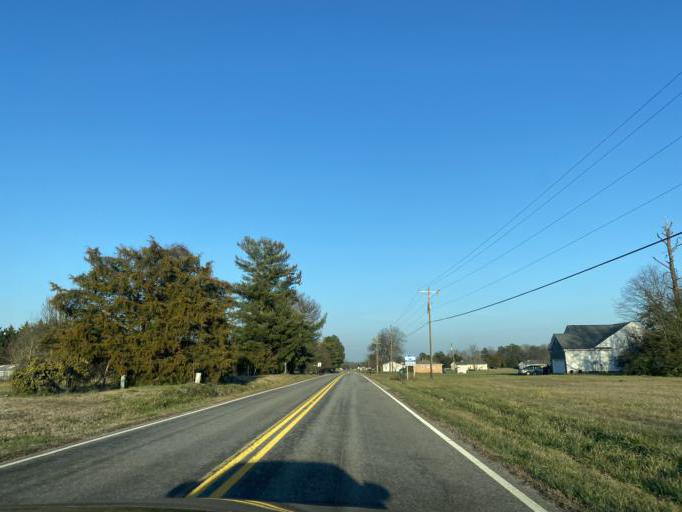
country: US
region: South Carolina
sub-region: Cherokee County
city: Gaffney
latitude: 35.1055
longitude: -81.6751
